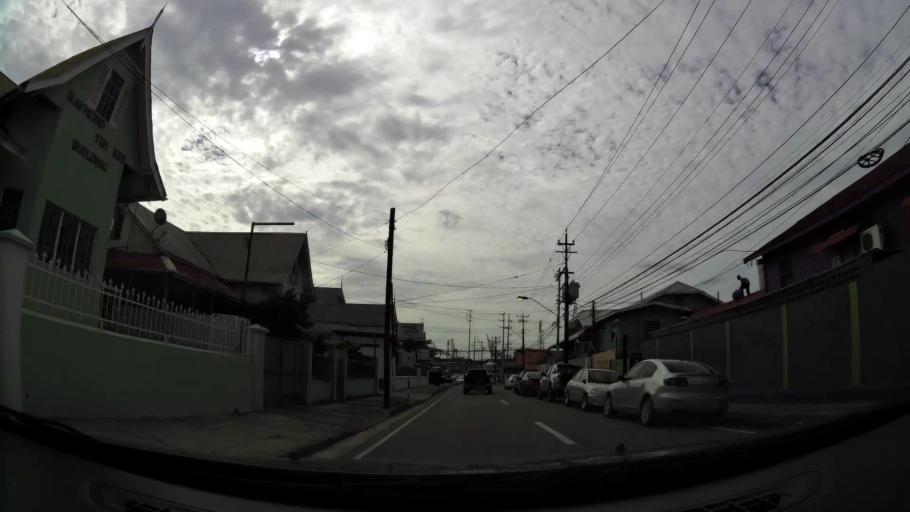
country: TT
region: City of Port of Spain
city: Port-of-Spain
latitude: 10.6549
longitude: -61.5167
